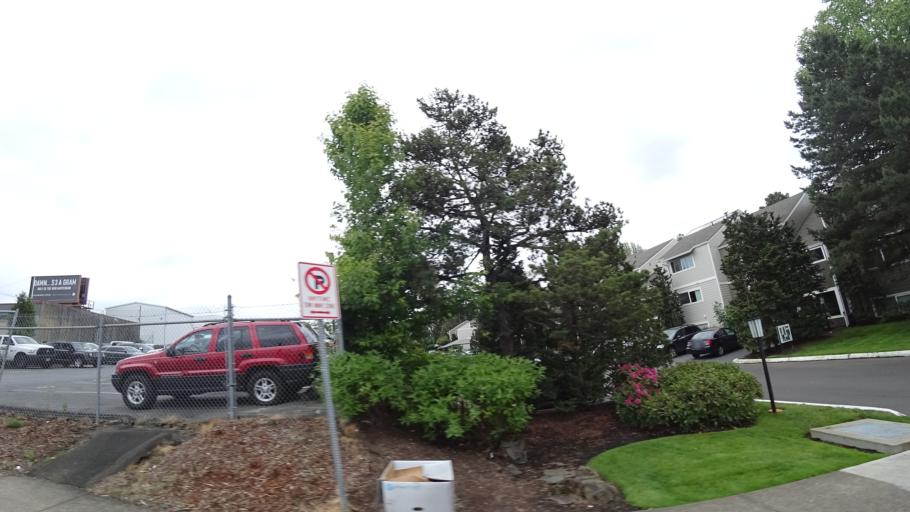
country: US
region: Oregon
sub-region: Washington County
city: Beaverton
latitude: 45.4913
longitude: -122.7868
